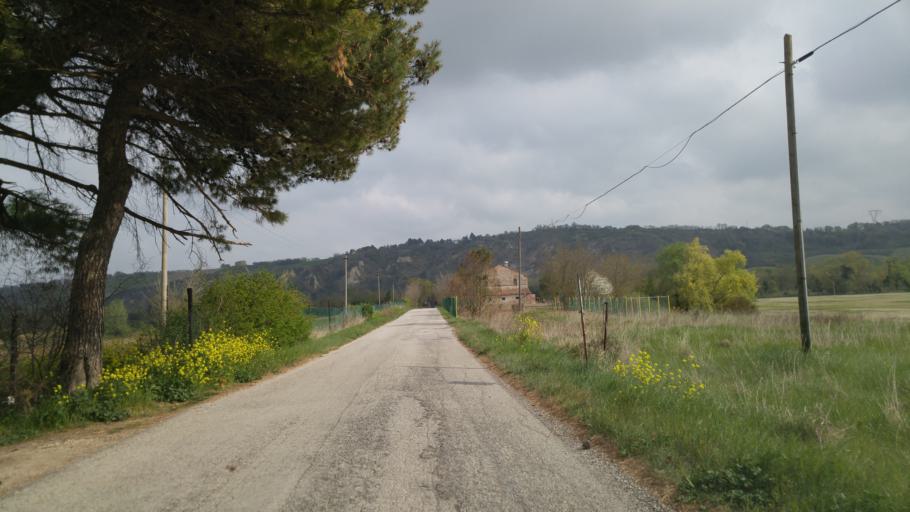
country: IT
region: The Marches
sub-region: Provincia di Pesaro e Urbino
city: Bellocchi
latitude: 43.7746
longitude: 12.9848
